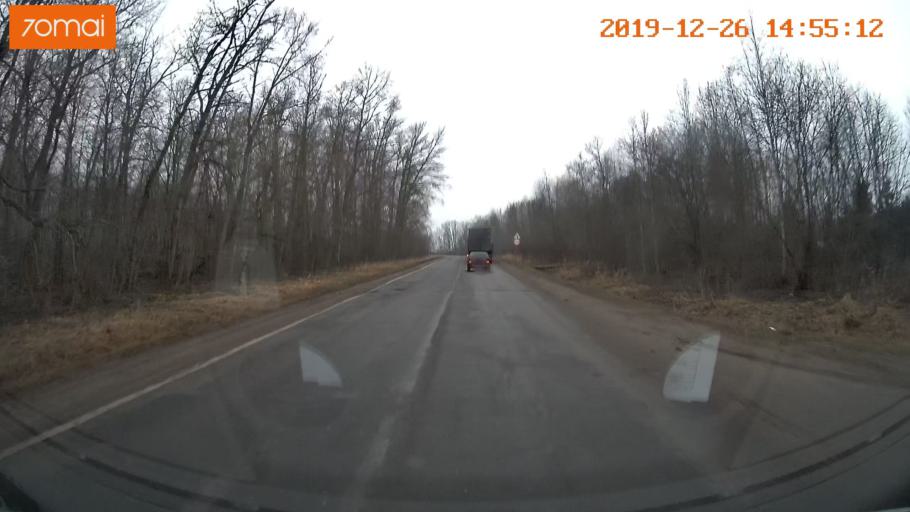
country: RU
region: Jaroslavl
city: Rybinsk
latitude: 58.3022
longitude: 38.8773
